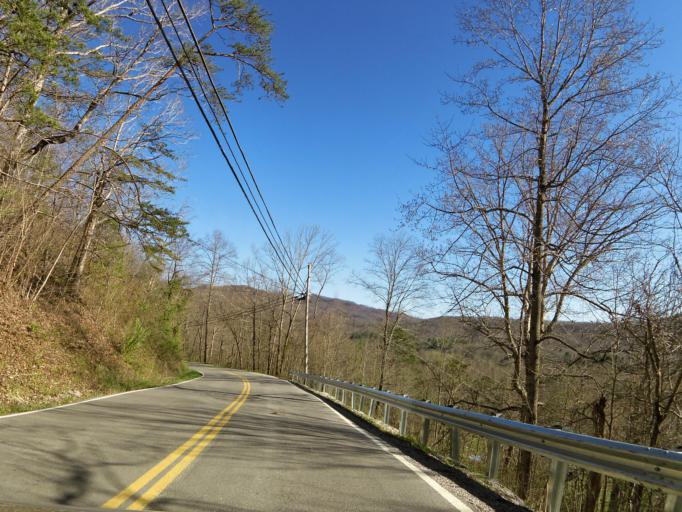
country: US
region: Tennessee
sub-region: Scott County
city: Huntsville
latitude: 36.3421
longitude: -84.3904
